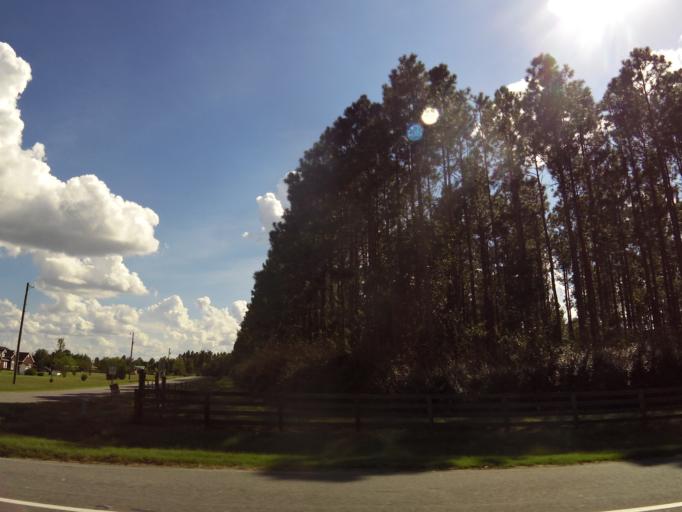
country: US
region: Georgia
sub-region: Lowndes County
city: Valdosta
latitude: 30.8070
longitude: -83.2129
